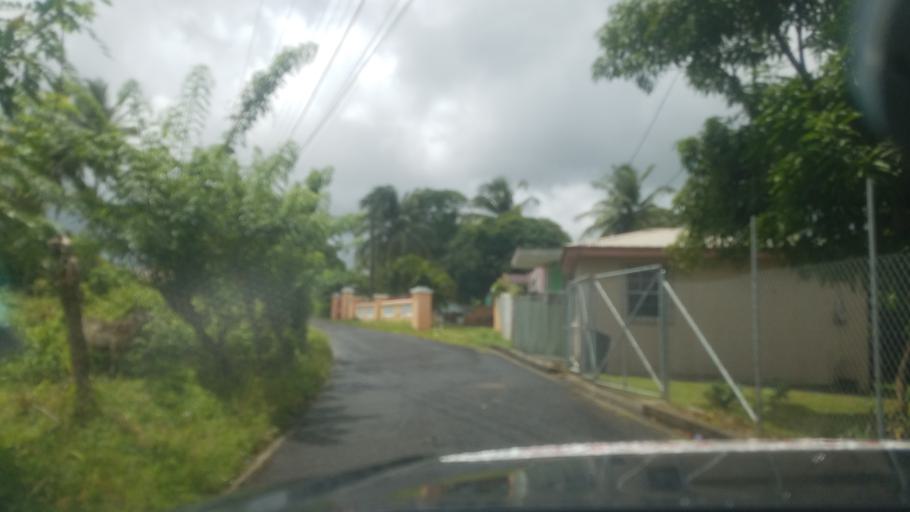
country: LC
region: Laborie Quarter
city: Laborie
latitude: 13.7587
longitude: -60.9760
